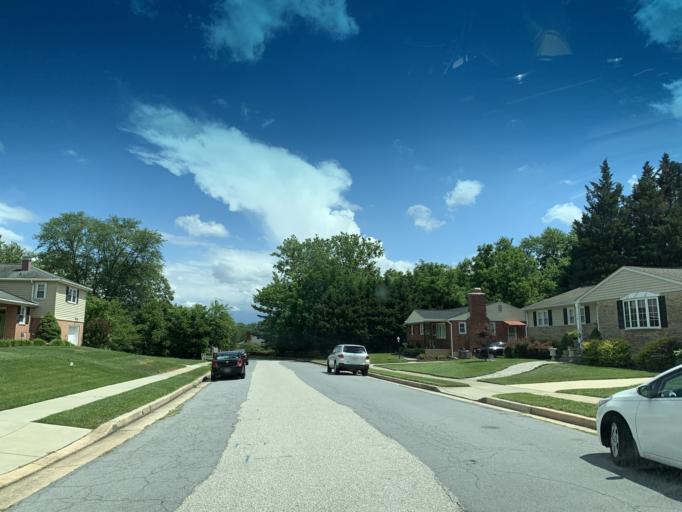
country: US
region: Maryland
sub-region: Baltimore County
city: Timonium
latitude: 39.4441
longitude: -76.6194
